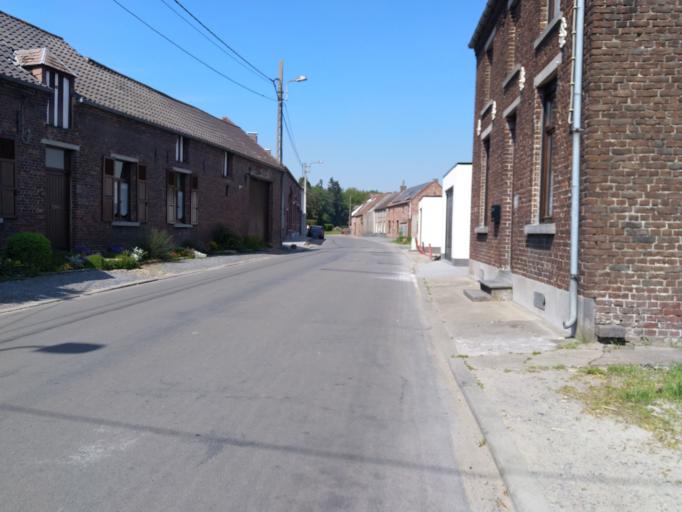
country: BE
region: Wallonia
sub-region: Province du Hainaut
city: Mons
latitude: 50.4484
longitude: 4.0112
